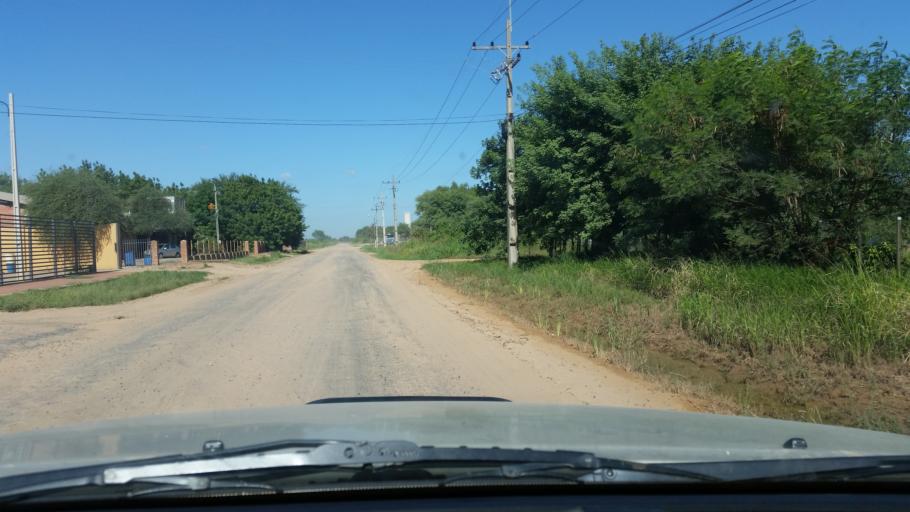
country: PY
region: Boqueron
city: Colonia Menno
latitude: -22.3980
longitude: -59.8394
